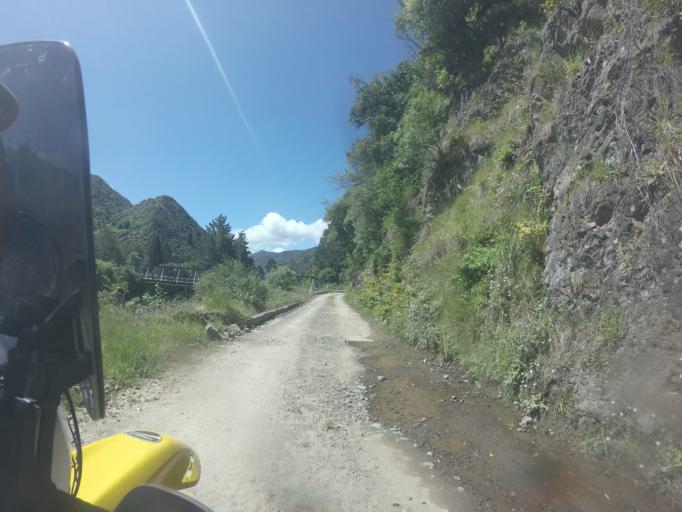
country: NZ
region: Bay of Plenty
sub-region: Opotiki District
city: Opotiki
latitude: -38.2948
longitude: 177.3385
